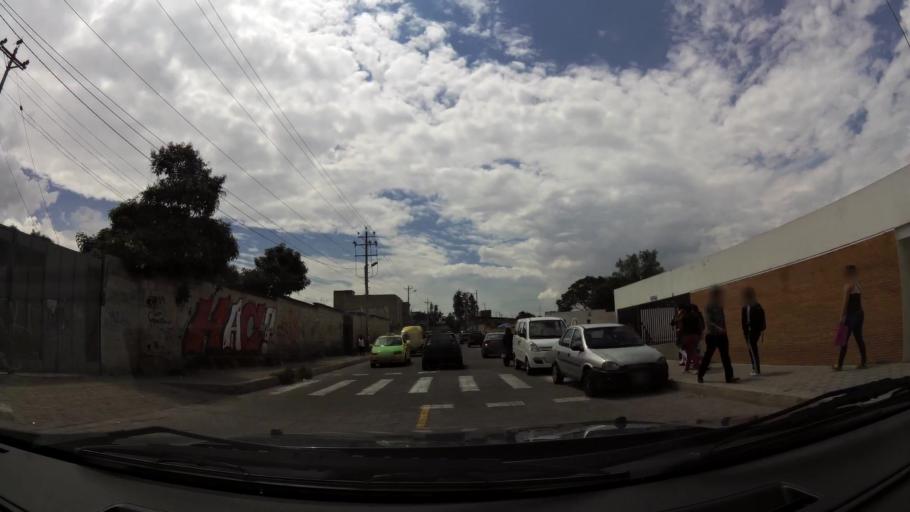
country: EC
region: Pichincha
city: Quito
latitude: -0.0754
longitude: -78.4168
